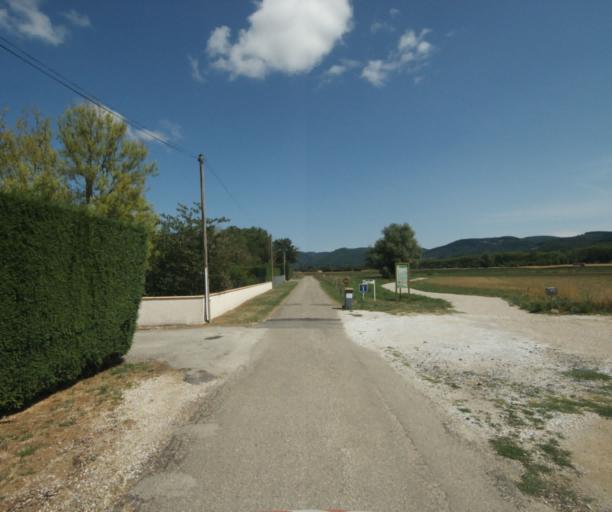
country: FR
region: Midi-Pyrenees
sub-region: Departement de la Haute-Garonne
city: Revel
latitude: 43.4578
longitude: 2.0194
